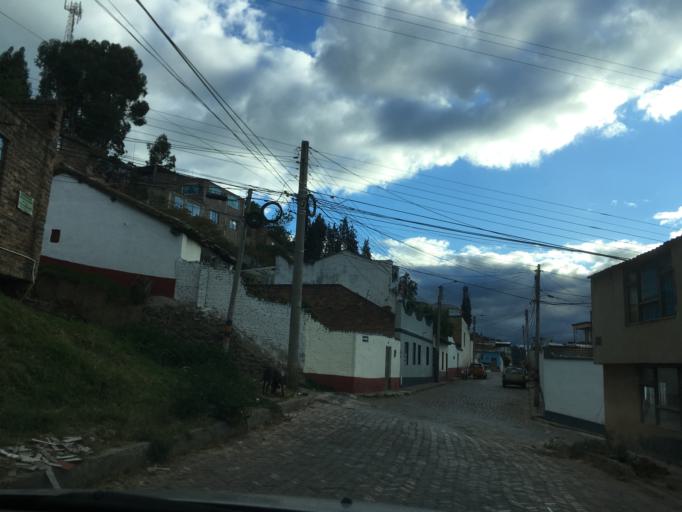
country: CO
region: Boyaca
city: Sogamoso
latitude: 5.7157
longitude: -72.9238
